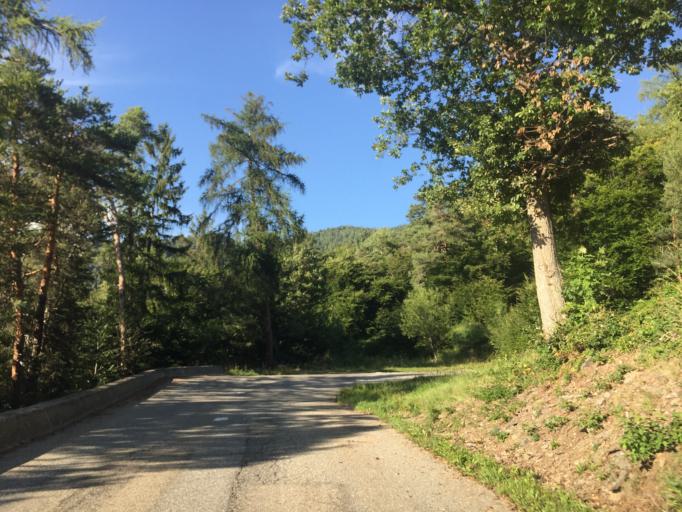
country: FR
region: Rhone-Alpes
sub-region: Departement de la Savoie
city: Moutiers
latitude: 45.5062
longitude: 6.5776
